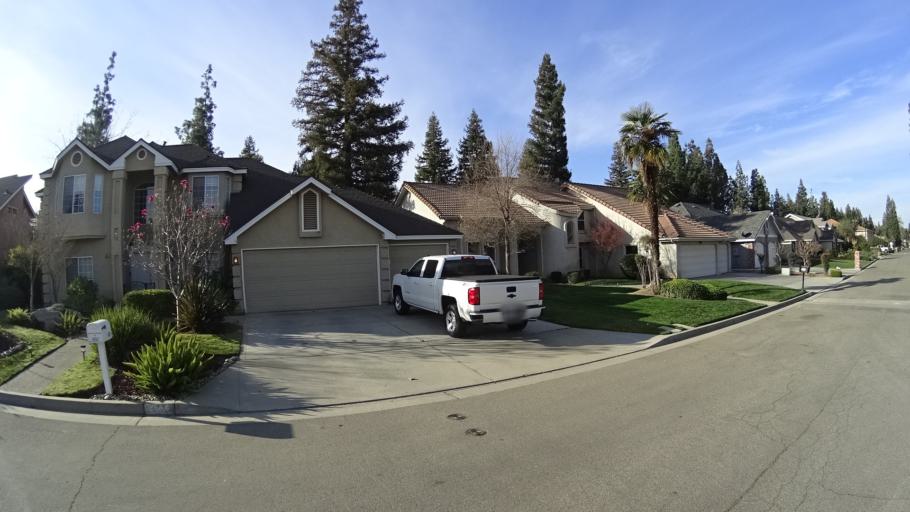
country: US
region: California
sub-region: Fresno County
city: Clovis
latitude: 36.8671
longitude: -119.7714
